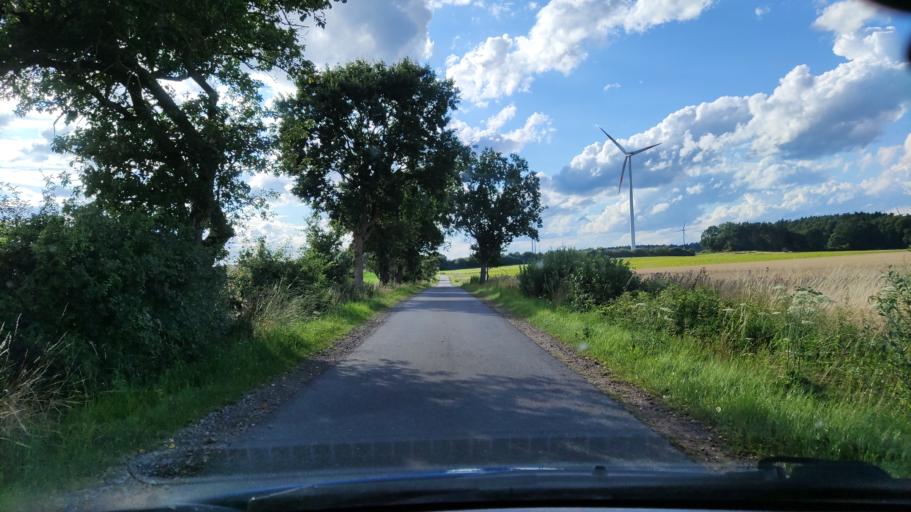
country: DE
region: Lower Saxony
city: Nahrendorf
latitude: 53.1768
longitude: 10.8028
